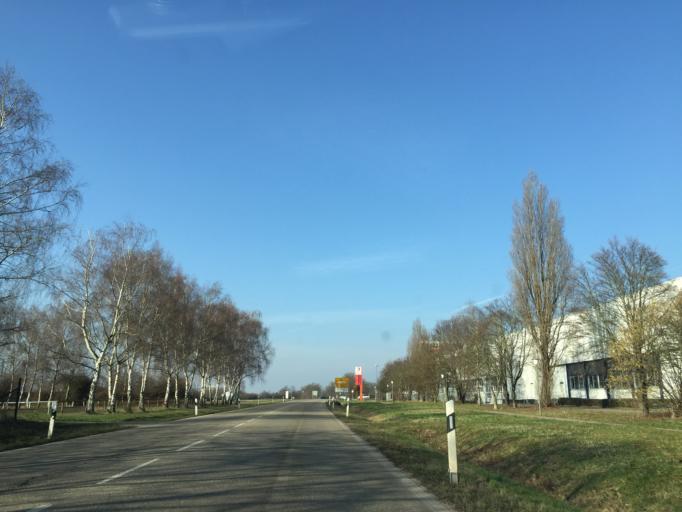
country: DE
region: Baden-Wuerttemberg
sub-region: Karlsruhe Region
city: Eppelheim
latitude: 49.4223
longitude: 8.6391
